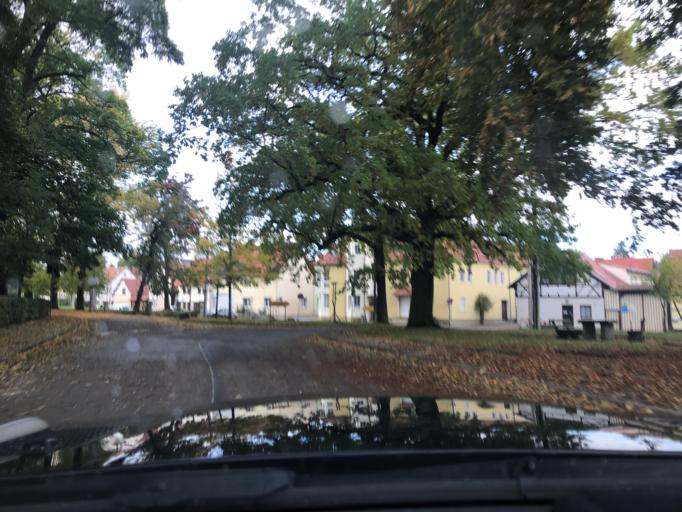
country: DE
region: Thuringia
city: Mulverstedt
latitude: 51.1198
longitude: 10.5069
